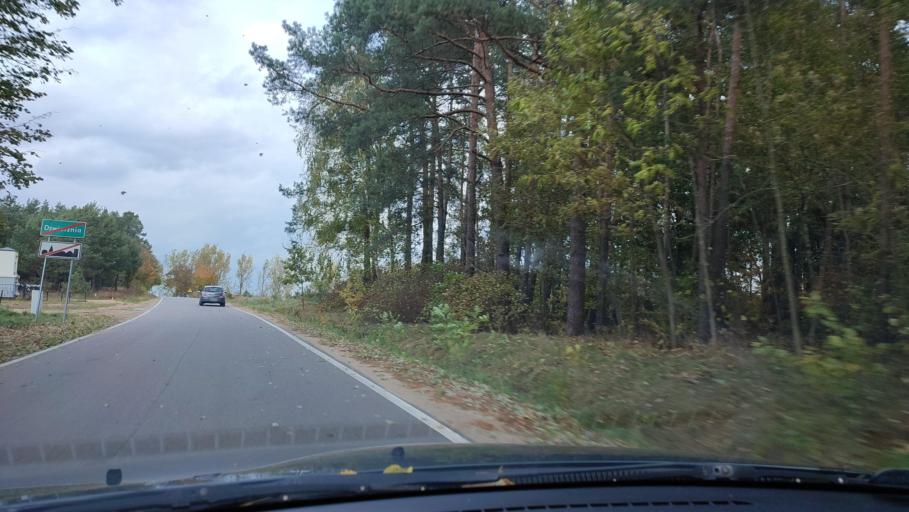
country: PL
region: Masovian Voivodeship
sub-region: Powiat mlawski
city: Mlawa
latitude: 53.1830
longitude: 20.3762
